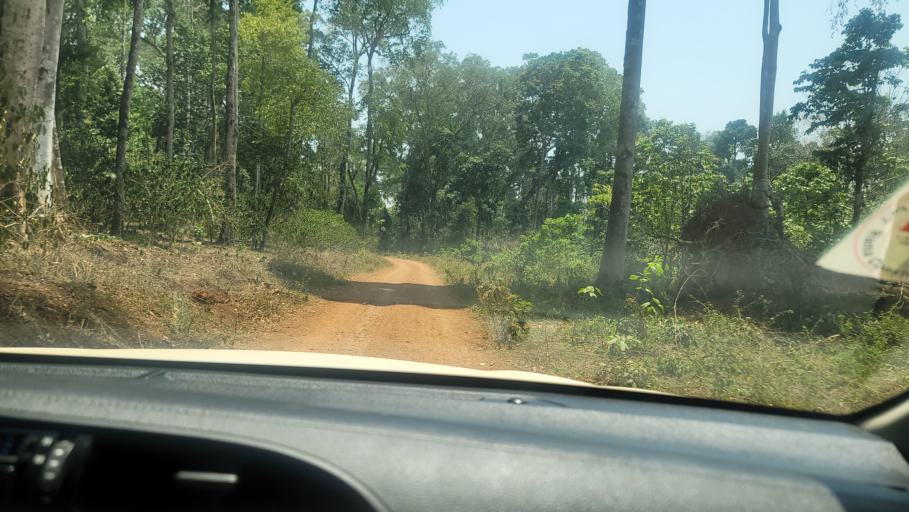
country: ET
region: Southern Nations, Nationalities, and People's Region
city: Bonga
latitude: 7.5083
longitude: 36.2261
